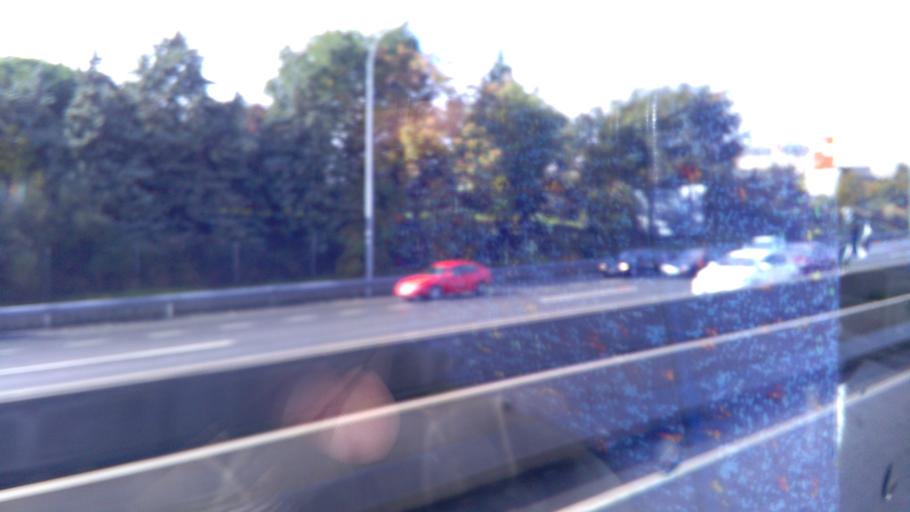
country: ES
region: Madrid
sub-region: Provincia de Madrid
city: Villaverde
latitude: 40.3639
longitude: -3.6888
